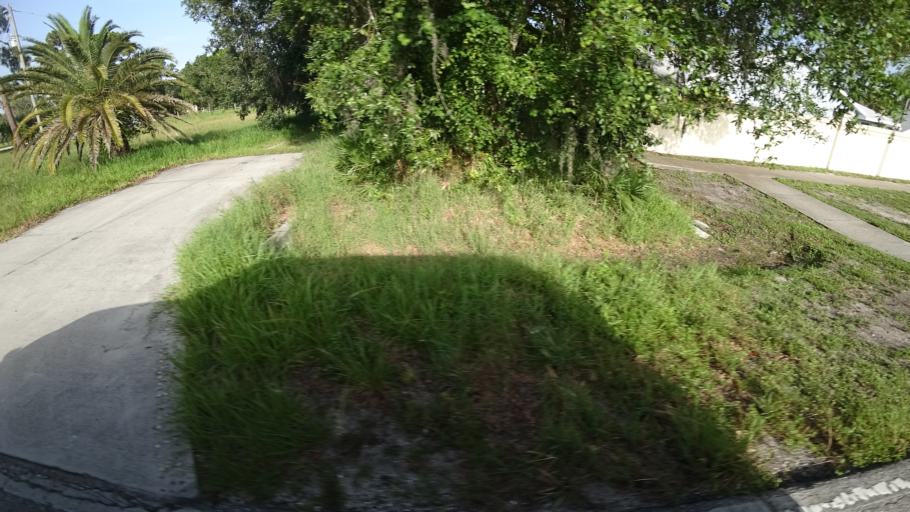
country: US
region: Florida
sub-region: Manatee County
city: Samoset
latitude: 27.4400
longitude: -82.4811
